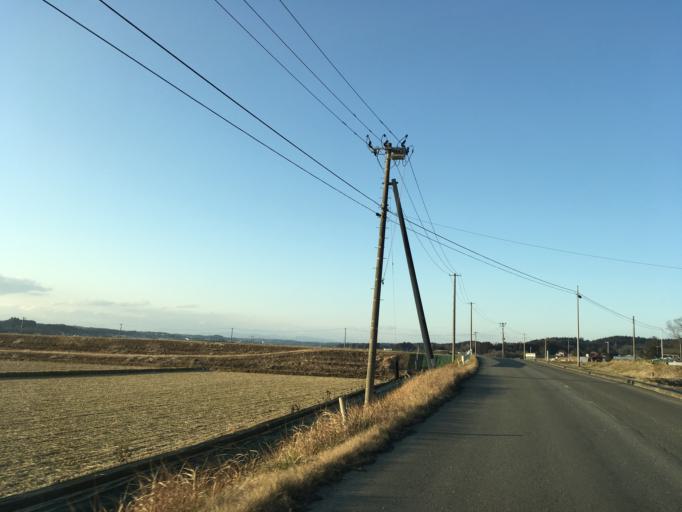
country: JP
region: Iwate
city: Ichinoseki
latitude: 38.8108
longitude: 141.2147
